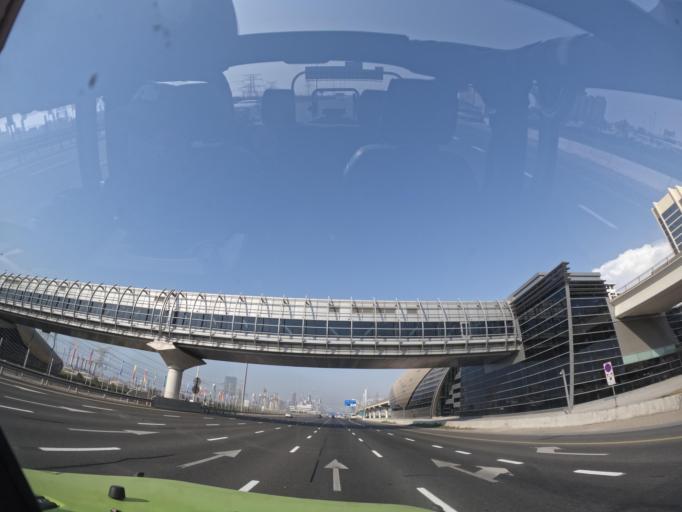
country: AE
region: Dubai
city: Dubai
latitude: 25.0477
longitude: 55.1167
